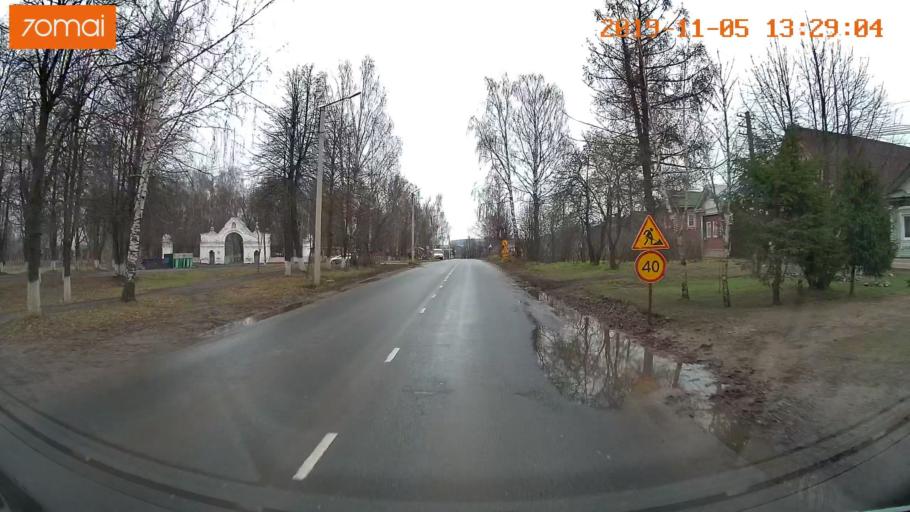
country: RU
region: Ivanovo
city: Shuya
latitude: 56.8584
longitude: 41.3946
